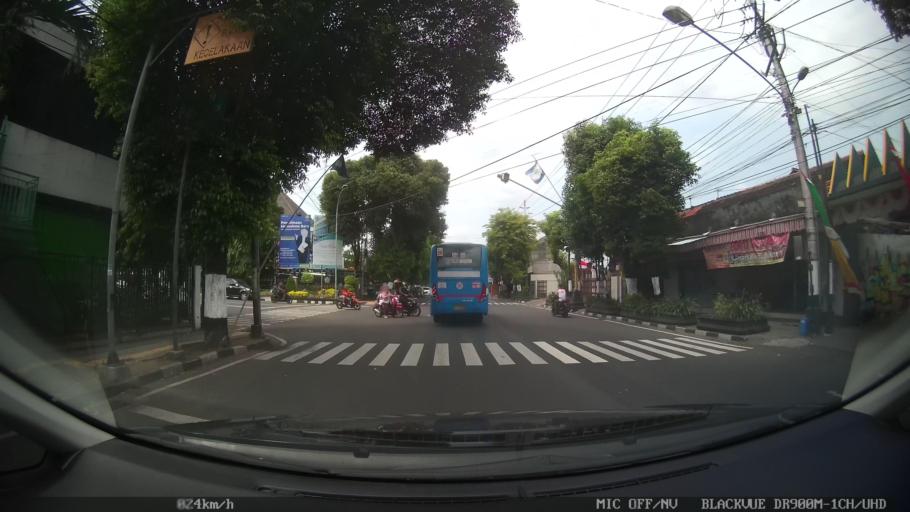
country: ID
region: Daerah Istimewa Yogyakarta
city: Yogyakarta
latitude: -7.8021
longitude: 110.3917
